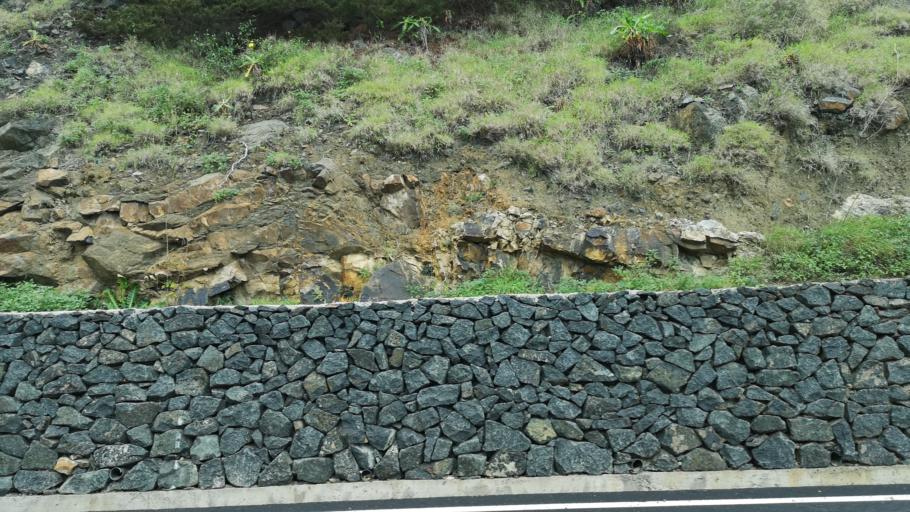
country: ES
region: Canary Islands
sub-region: Provincia de Santa Cruz de Tenerife
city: Agulo
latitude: 28.1873
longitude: -17.2143
